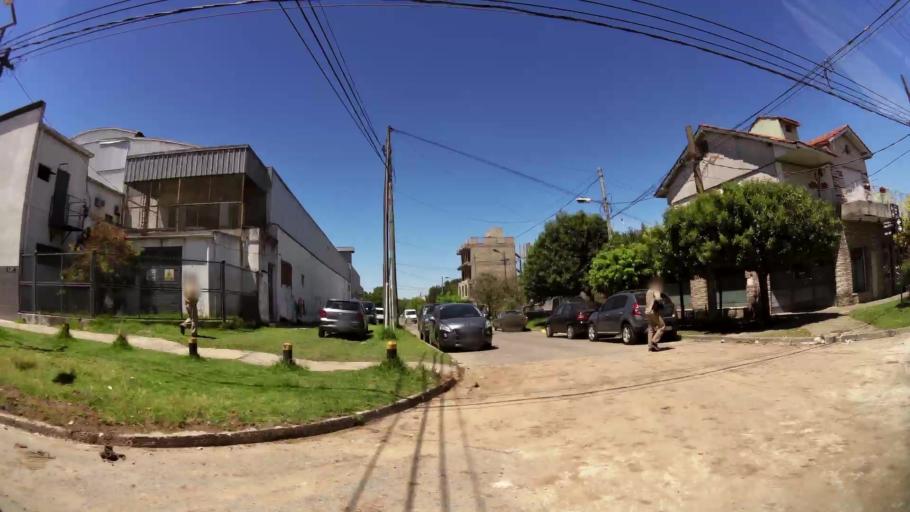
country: AR
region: Buenos Aires
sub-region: Partido de Quilmes
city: Quilmes
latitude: -34.7332
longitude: -58.2898
